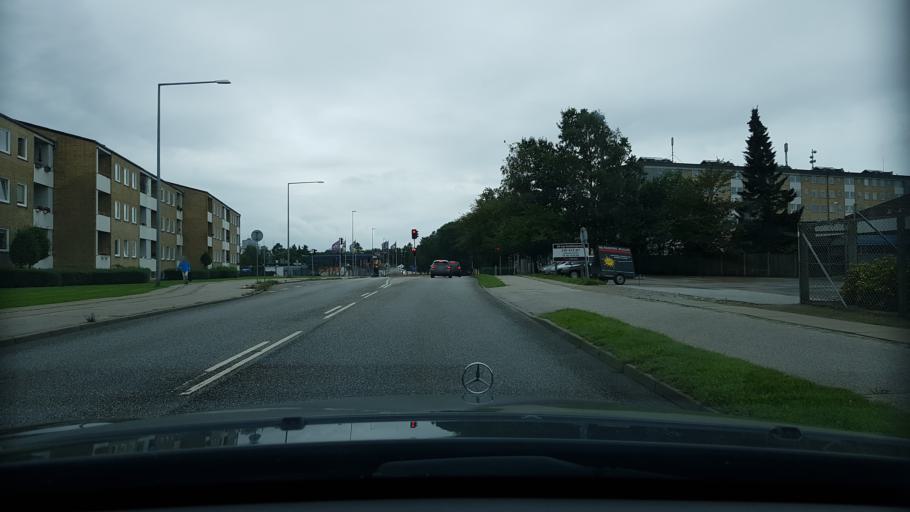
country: DK
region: Central Jutland
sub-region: Randers Kommune
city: Randers
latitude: 56.4810
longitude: 10.0416
